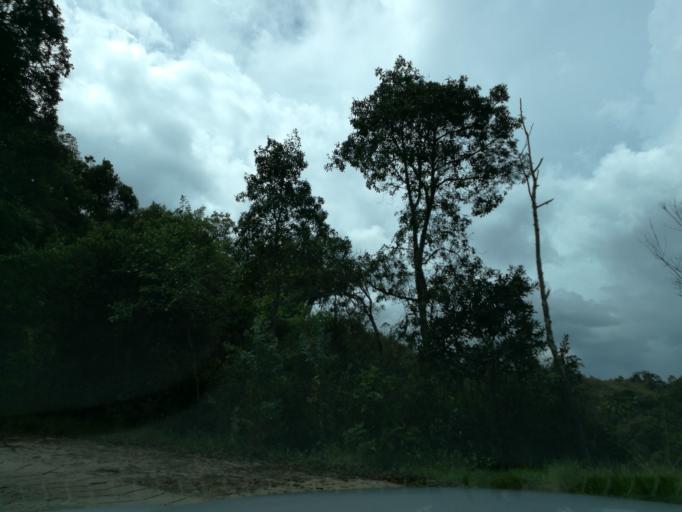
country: CO
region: Boyaca
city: Arcabuco
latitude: 5.7546
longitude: -73.4532
